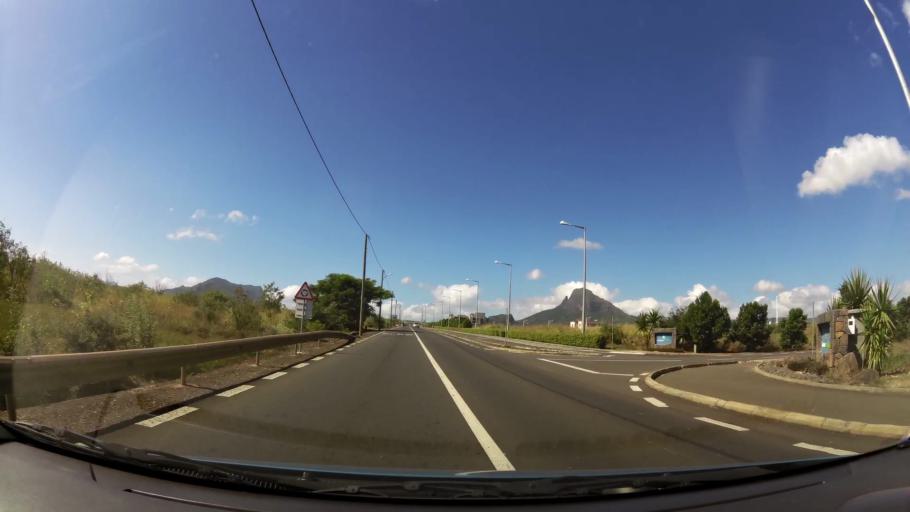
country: MU
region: Black River
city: Flic en Flac
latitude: -20.2770
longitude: 57.3830
